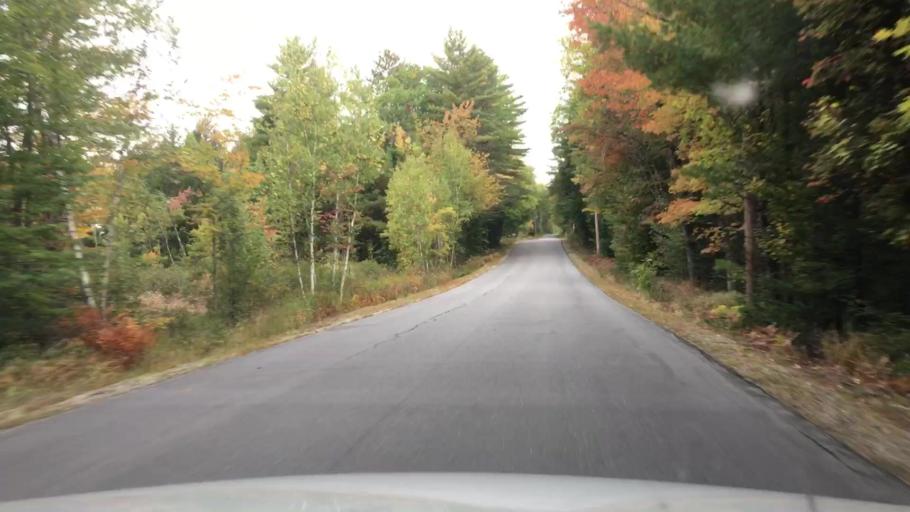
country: US
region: Maine
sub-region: Cumberland County
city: Harrison
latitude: 44.2452
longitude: -70.7195
